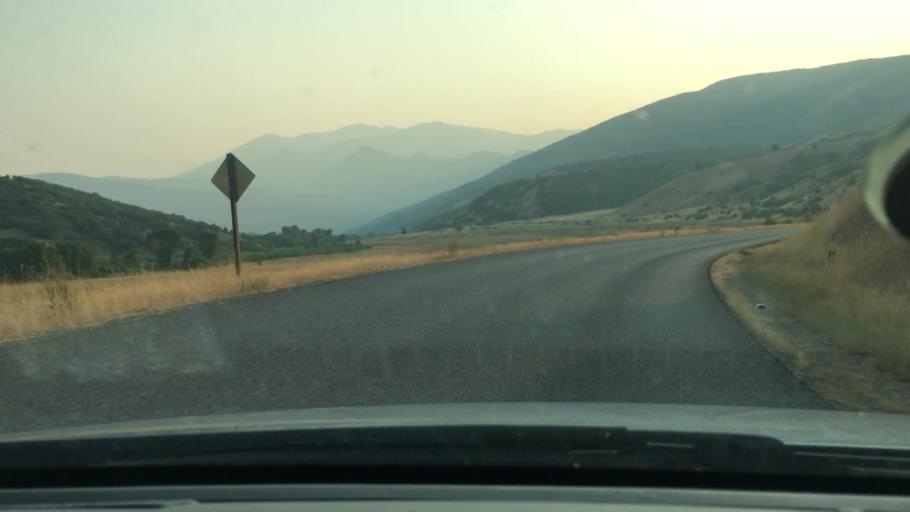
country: US
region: Utah
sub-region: Utah County
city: Mapleton
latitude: 40.0462
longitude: -111.4695
